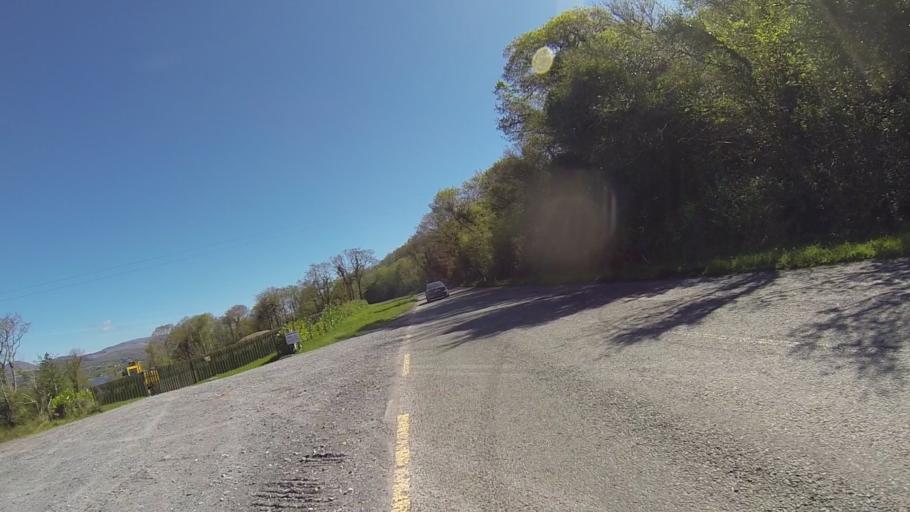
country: IE
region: Munster
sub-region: Ciarrai
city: Kenmare
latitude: 51.8573
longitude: -9.6209
